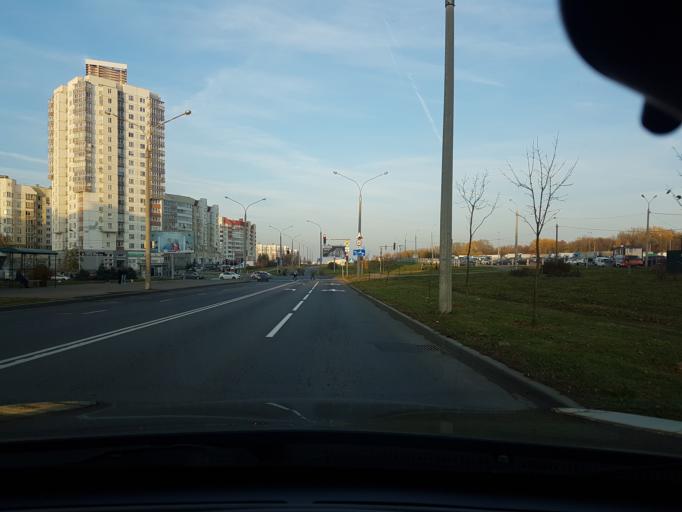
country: BY
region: Minsk
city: Shchomyslitsa
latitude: 53.8456
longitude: 27.4862
